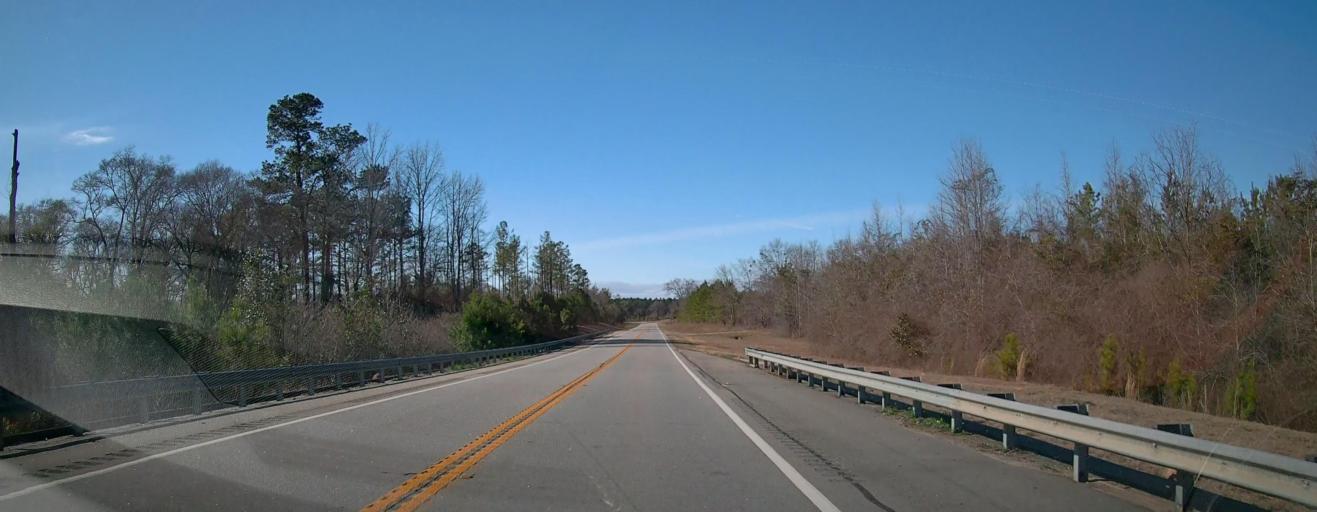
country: US
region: Georgia
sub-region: Macon County
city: Oglethorpe
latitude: 32.3468
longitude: -84.1451
